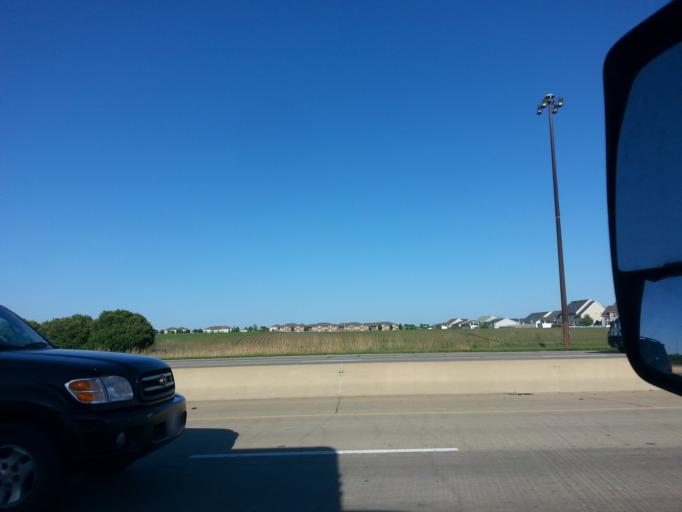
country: US
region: Illinois
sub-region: McLean County
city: Normal
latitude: 40.5295
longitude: -89.0276
